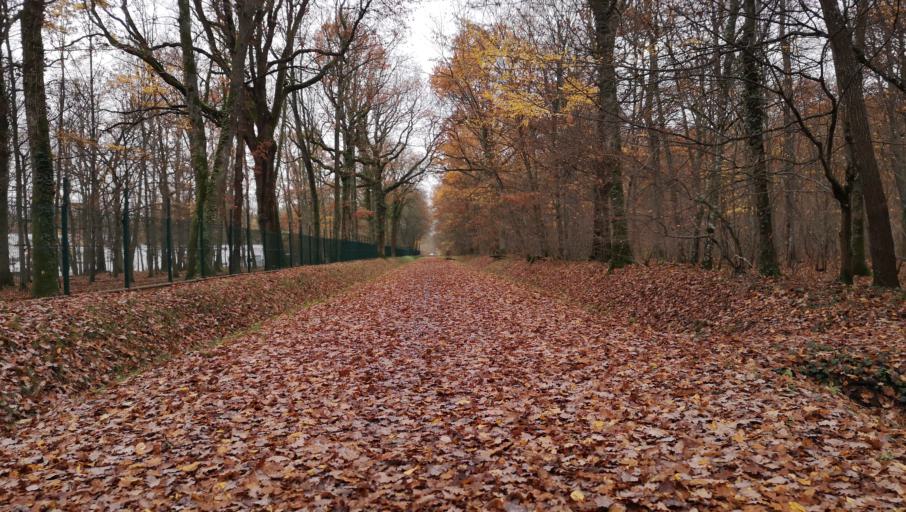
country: FR
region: Centre
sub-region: Departement du Loiret
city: Saint-Jean-de-Braye
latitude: 47.9288
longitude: 1.9870
